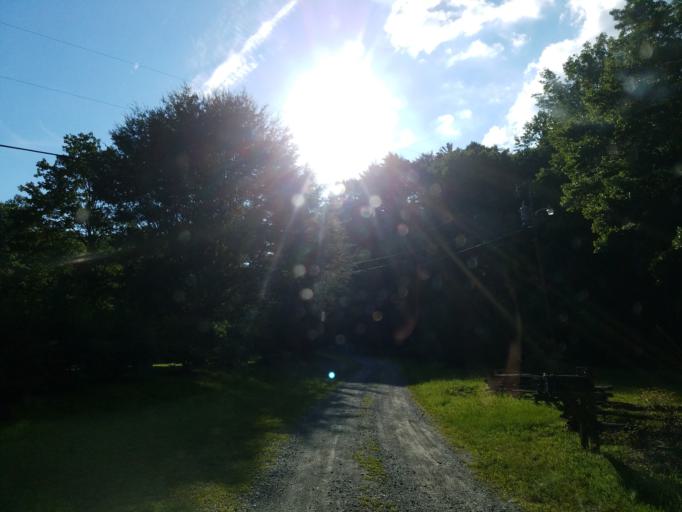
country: US
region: Georgia
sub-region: Dawson County
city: Dawsonville
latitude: 34.6266
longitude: -84.2440
